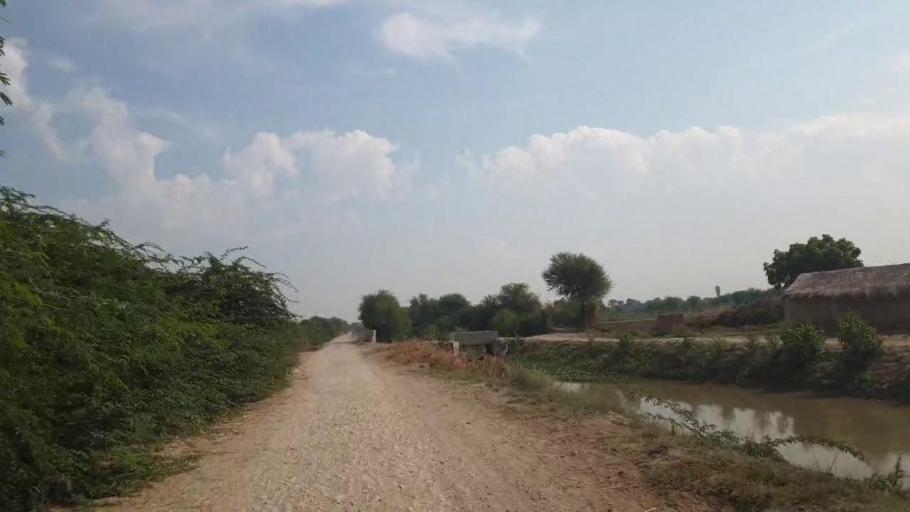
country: PK
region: Sindh
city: Tando Bago
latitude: 24.9279
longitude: 69.0119
